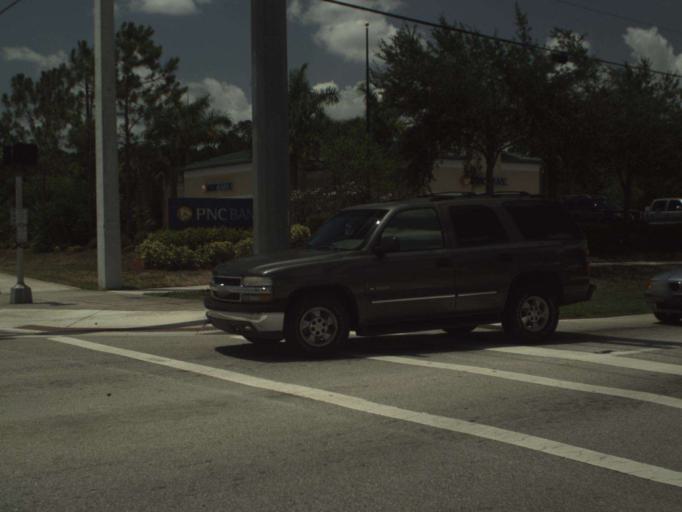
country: US
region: Florida
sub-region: Saint Lucie County
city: Port Saint Lucie
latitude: 27.2626
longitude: -80.3883
